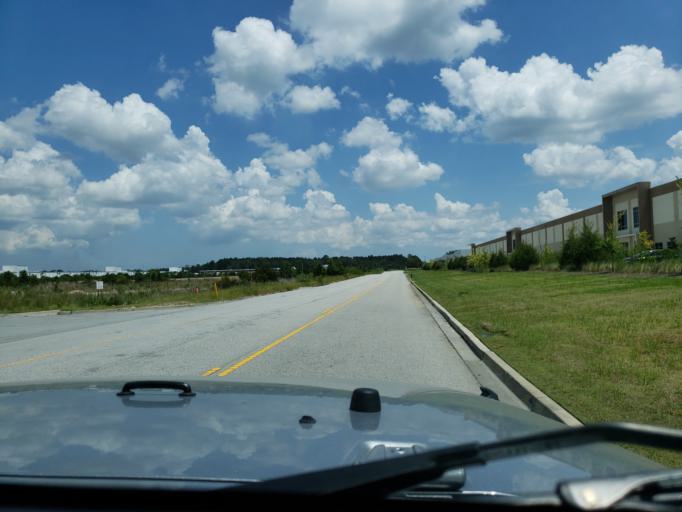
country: US
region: Georgia
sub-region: Chatham County
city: Bloomingdale
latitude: 32.1141
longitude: -81.2898
